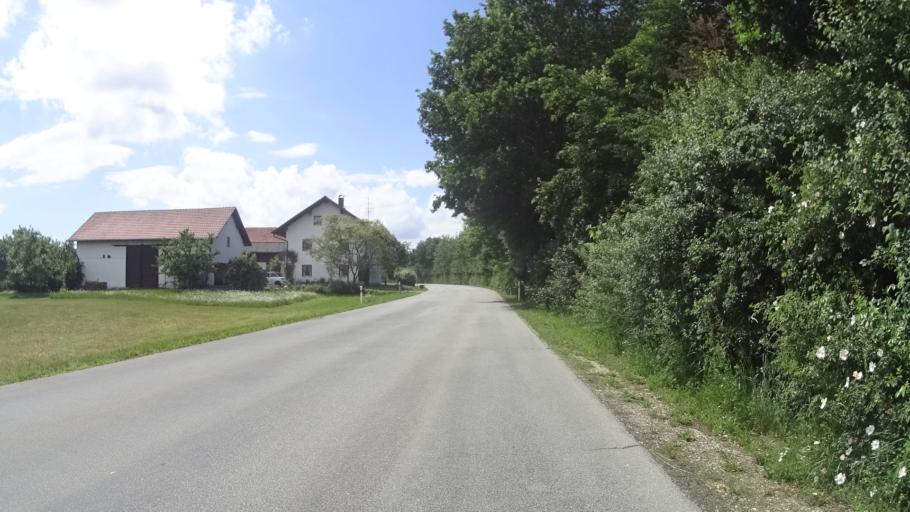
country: DE
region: Bavaria
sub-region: Lower Bavaria
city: Unterdietfurt
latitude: 48.3956
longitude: 12.6906
